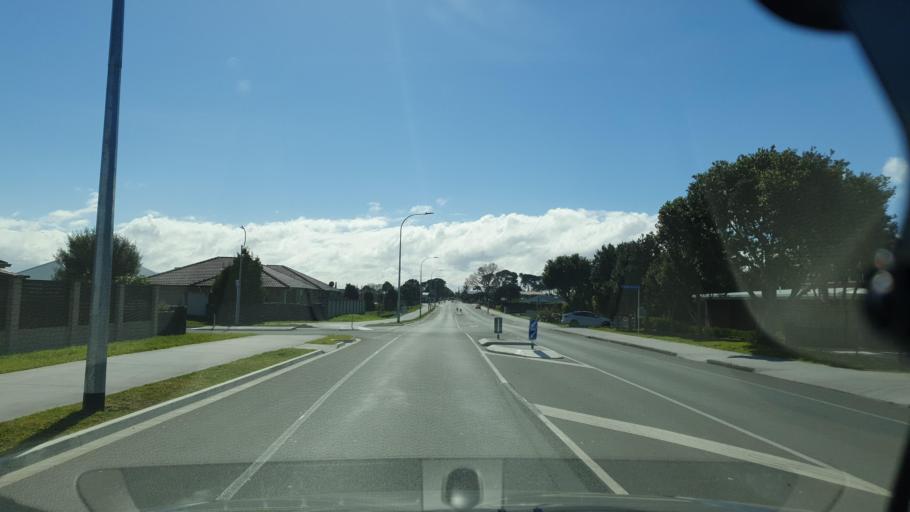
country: NZ
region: Bay of Plenty
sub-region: Tauranga City
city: Tauranga
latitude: -37.7047
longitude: 176.2847
